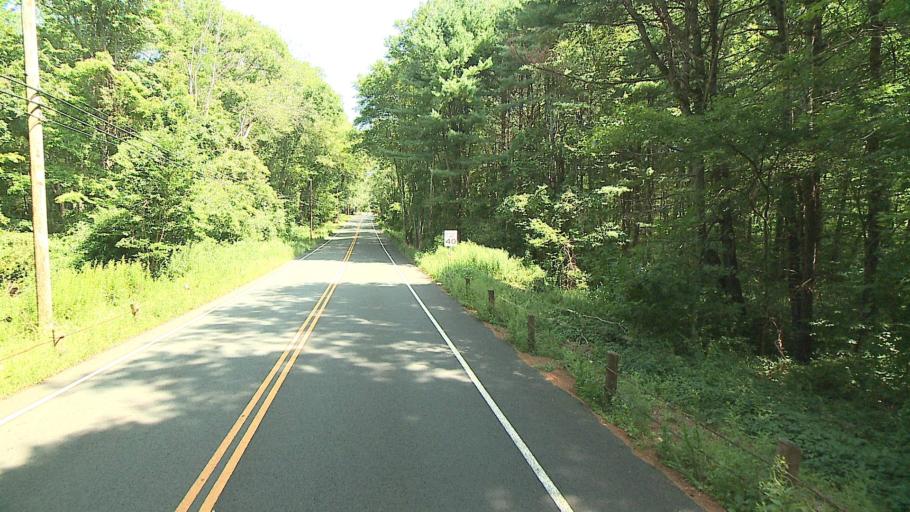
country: US
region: Connecticut
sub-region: Fairfield County
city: Newtown
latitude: 41.3187
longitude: -73.2735
